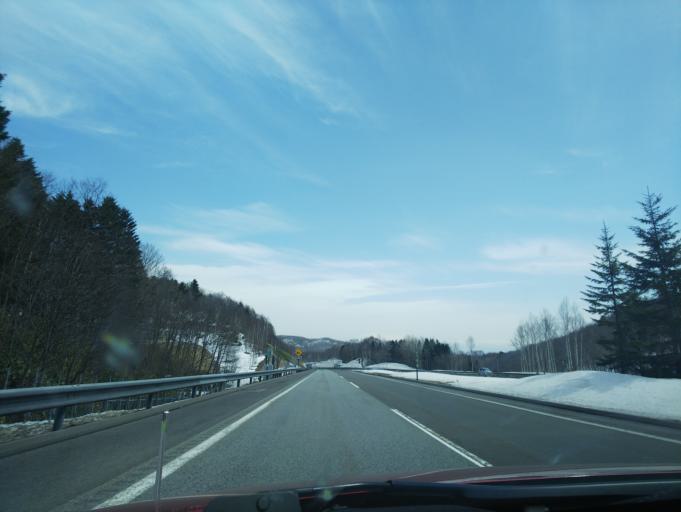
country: JP
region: Hokkaido
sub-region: Asahikawa-shi
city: Asahikawa
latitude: 43.7925
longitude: 142.2673
